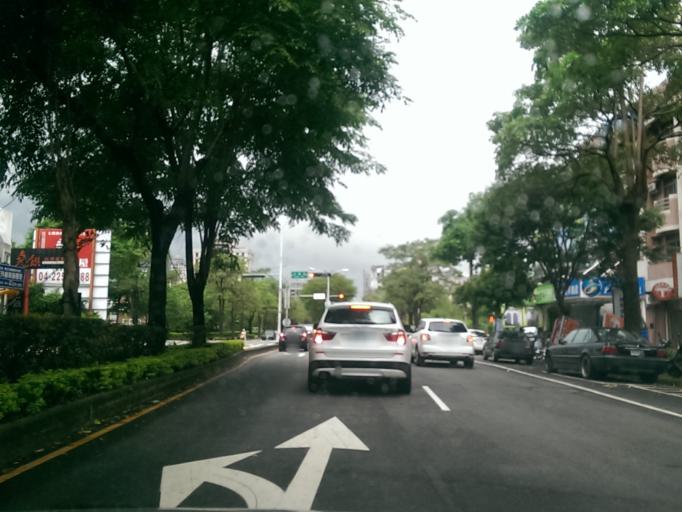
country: TW
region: Taiwan
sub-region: Taichung City
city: Taichung
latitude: 24.1543
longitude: 120.6407
